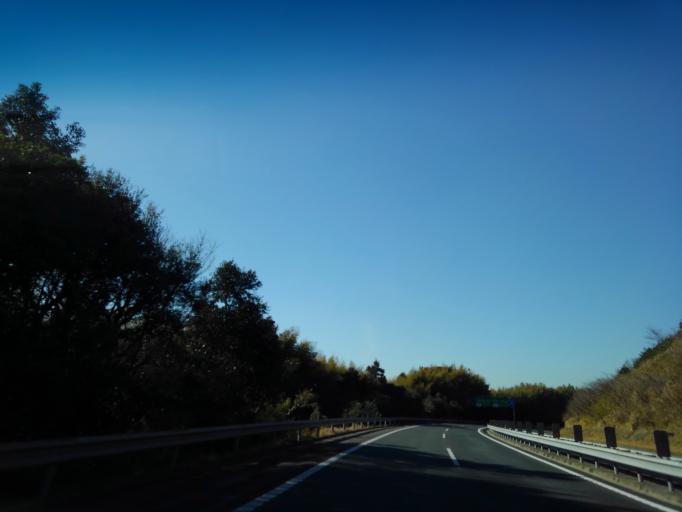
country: JP
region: Chiba
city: Kisarazu
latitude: 35.3509
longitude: 139.9336
